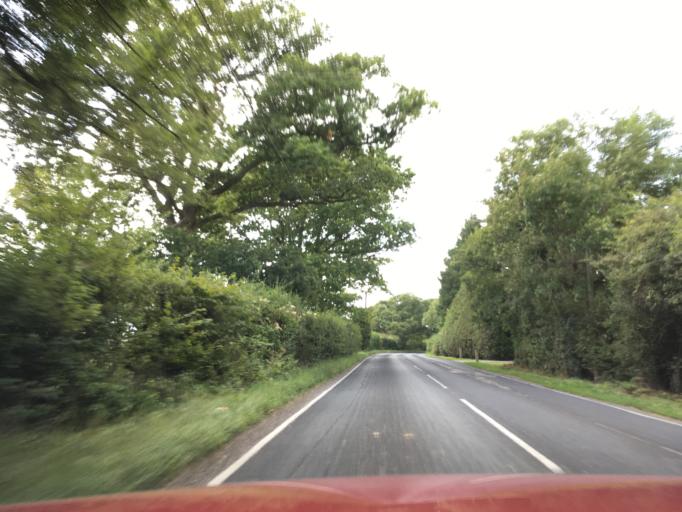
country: GB
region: England
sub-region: Kent
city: Tenterden
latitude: 51.0995
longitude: 0.6688
